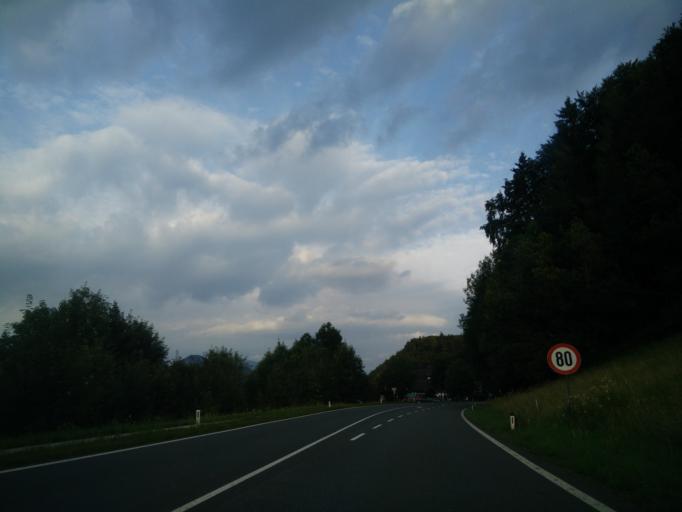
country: AT
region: Salzburg
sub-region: Politischer Bezirk Salzburg-Umgebung
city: Thalgau
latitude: 47.8118
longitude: 13.2446
